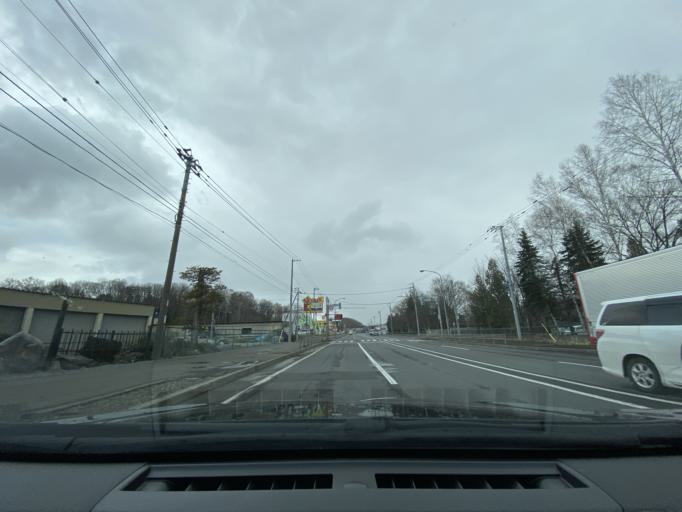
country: JP
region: Hokkaido
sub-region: Asahikawa-shi
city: Asahikawa
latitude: 43.7688
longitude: 142.2857
